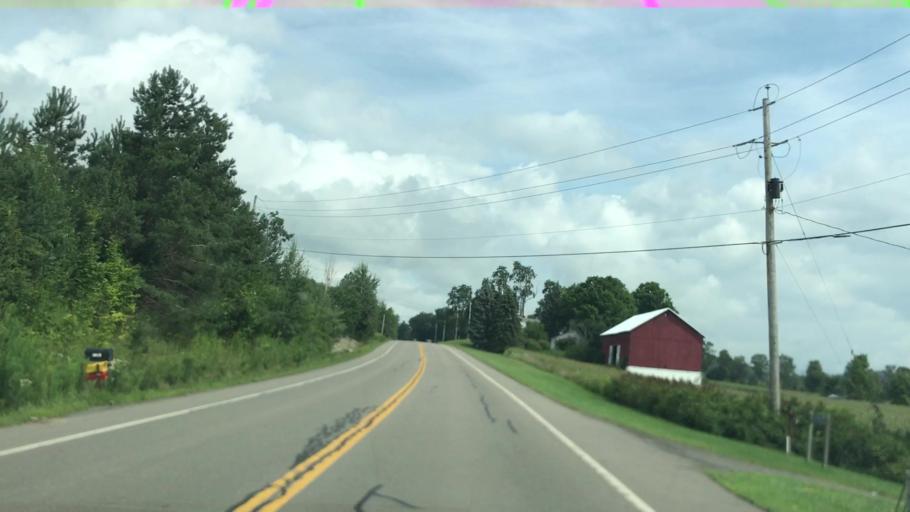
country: US
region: New York
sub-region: Ontario County
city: Naples
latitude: 42.5033
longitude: -77.2858
